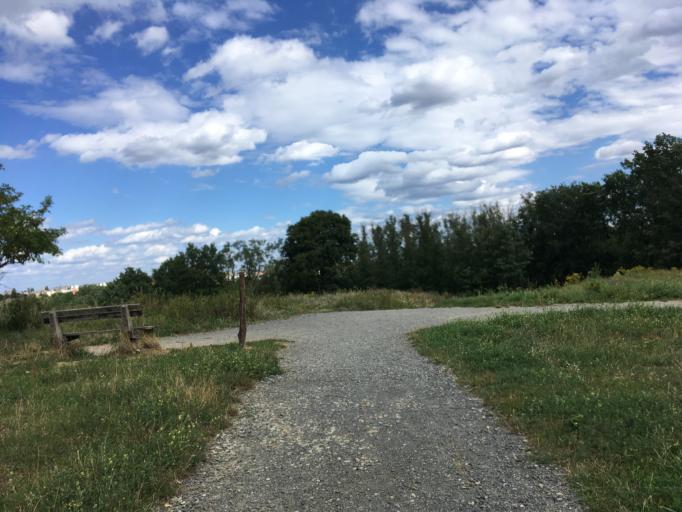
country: DE
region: Berlin
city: Staaken
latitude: 52.5215
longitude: 13.1417
